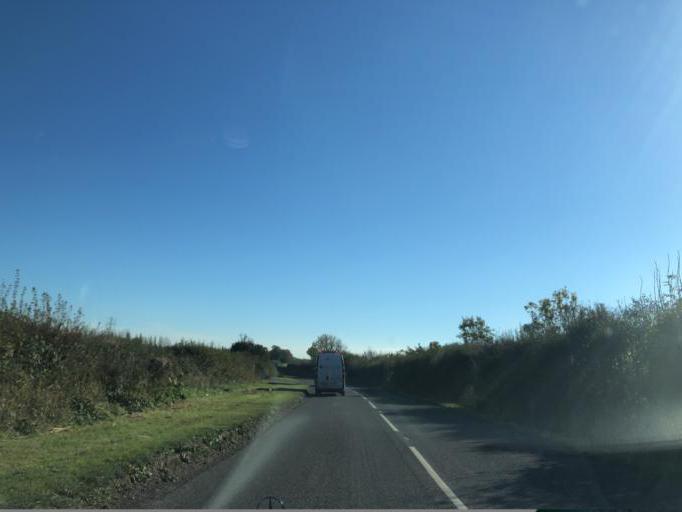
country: GB
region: England
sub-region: Warwickshire
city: Royal Leamington Spa
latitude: 52.2555
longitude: -1.5262
